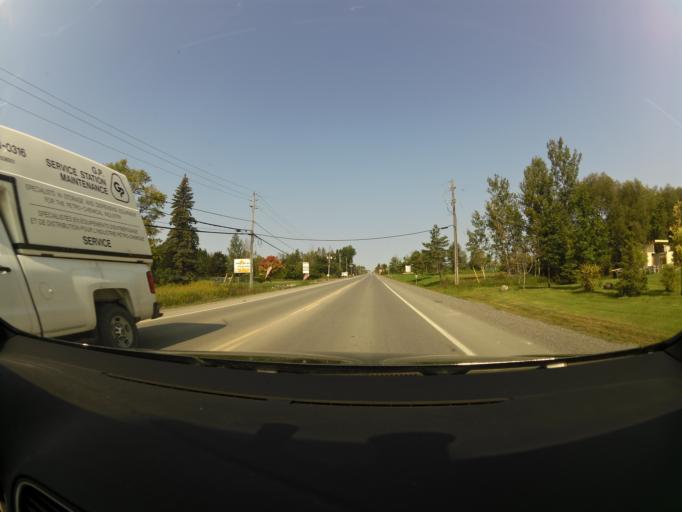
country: CA
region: Ontario
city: Bells Corners
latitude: 45.3031
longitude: -75.9843
